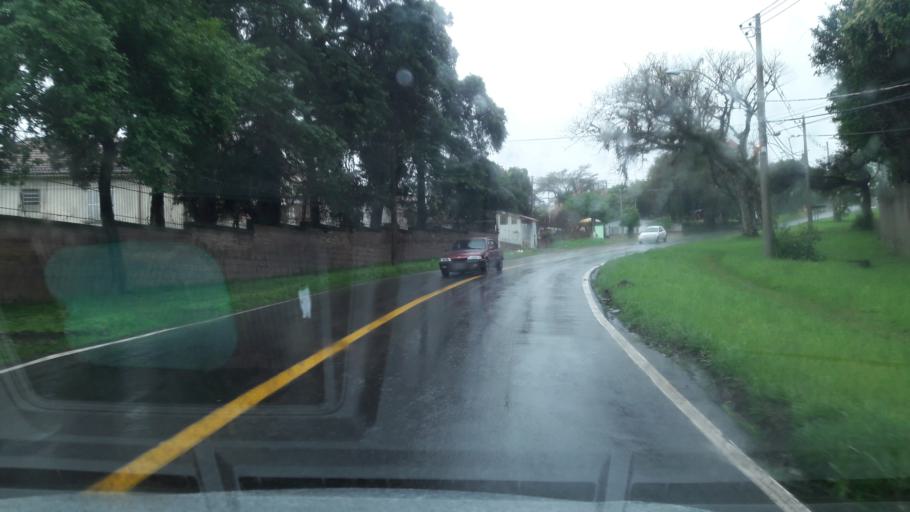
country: BR
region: Rio Grande do Sul
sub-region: Porto Alegre
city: Porto Alegre
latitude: -30.1294
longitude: -51.2235
